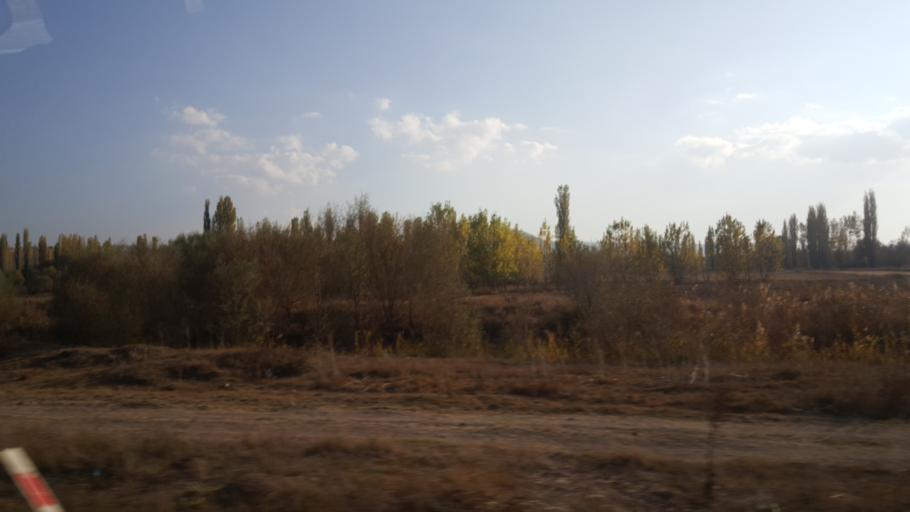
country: TR
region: Eskisehir
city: Seyitgazi
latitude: 39.4161
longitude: 30.6347
